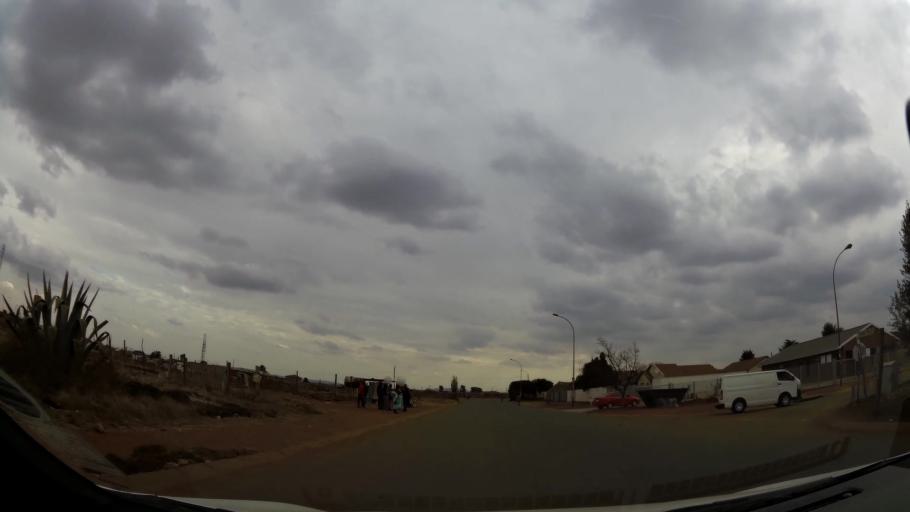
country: ZA
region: Gauteng
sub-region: Ekurhuleni Metropolitan Municipality
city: Germiston
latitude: -26.3972
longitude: 28.1487
